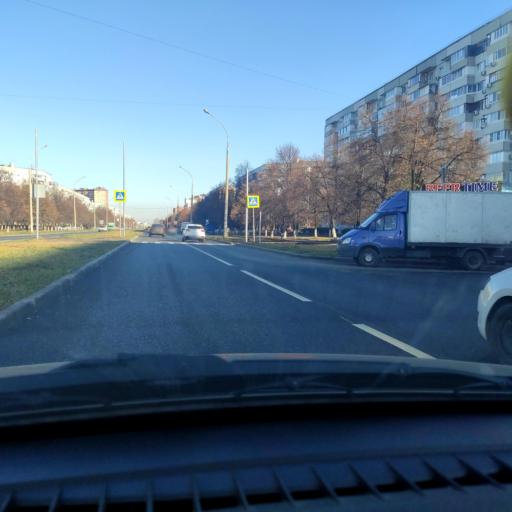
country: RU
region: Samara
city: Tol'yatti
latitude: 53.5350
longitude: 49.3290
